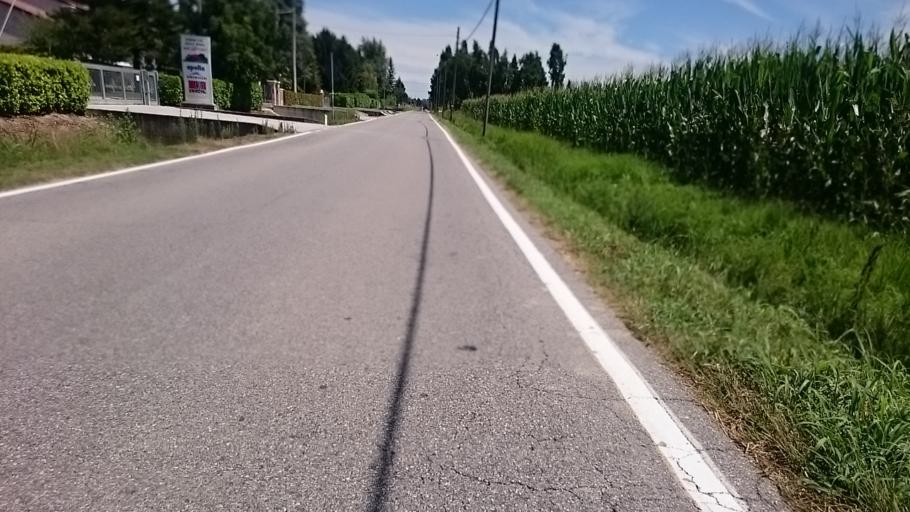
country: IT
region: Veneto
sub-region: Provincia di Padova
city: Villanova
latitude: 45.5026
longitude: 11.9749
